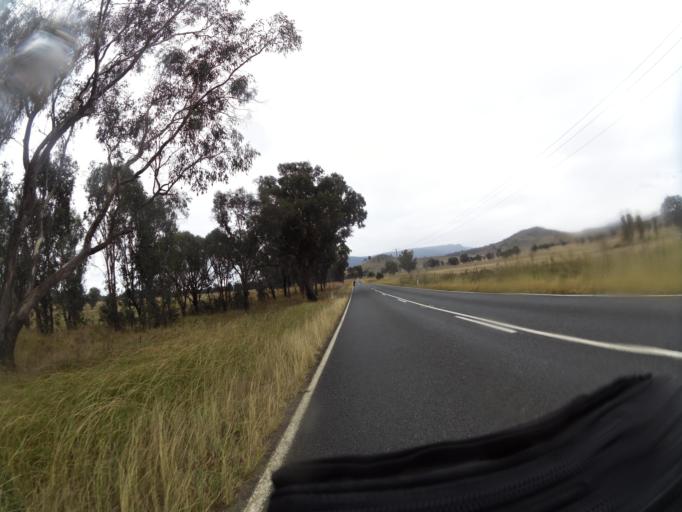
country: AU
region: New South Wales
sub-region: Greater Hume Shire
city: Holbrook
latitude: -36.2117
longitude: 147.8171
